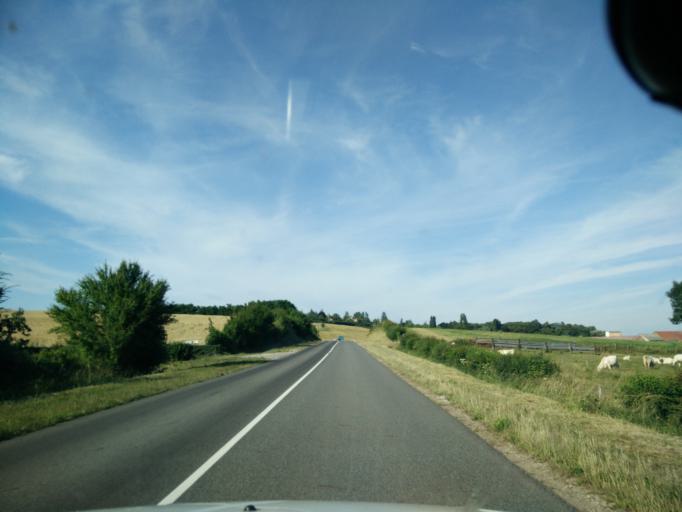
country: FR
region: Auvergne
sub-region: Departement de l'Allier
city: Souvigny
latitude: 46.5307
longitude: 3.1806
